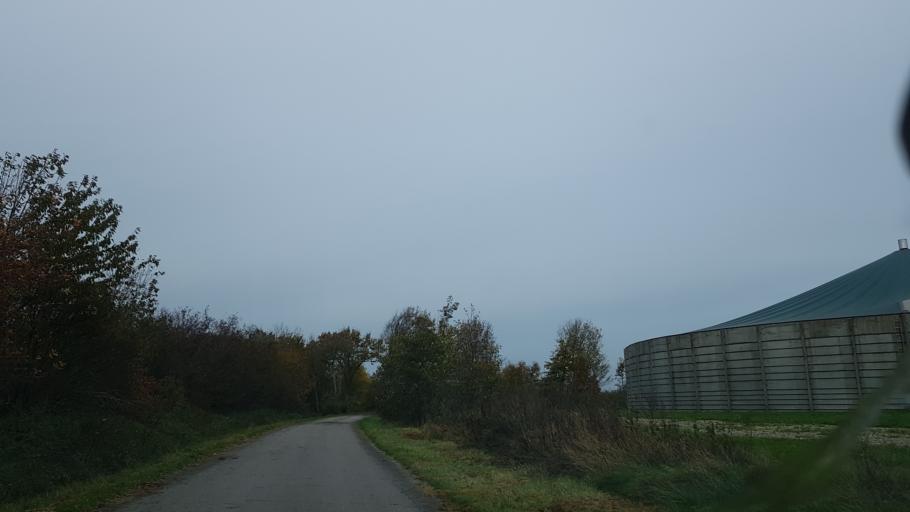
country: DK
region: South Denmark
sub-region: Tonder Kommune
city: Sherrebek
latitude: 55.2171
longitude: 8.8663
